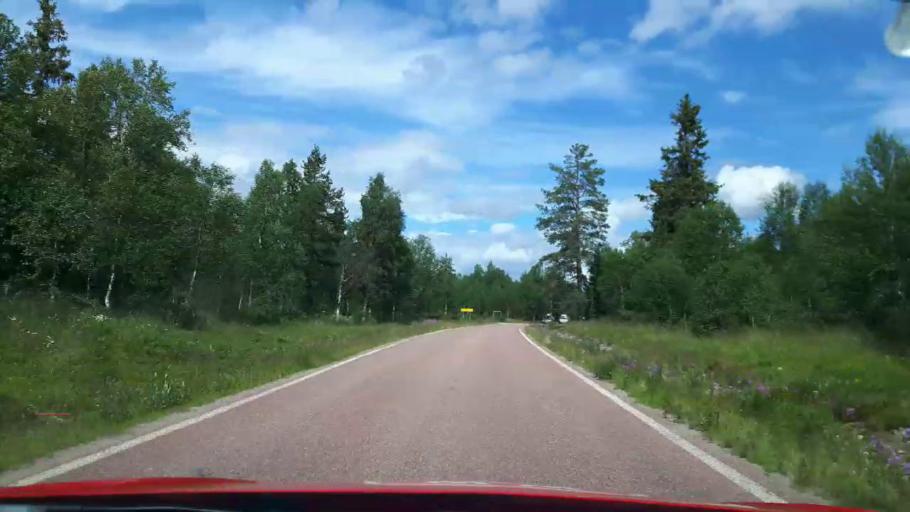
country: NO
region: Hedmark
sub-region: Trysil
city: Innbygda
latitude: 62.0088
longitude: 12.9754
